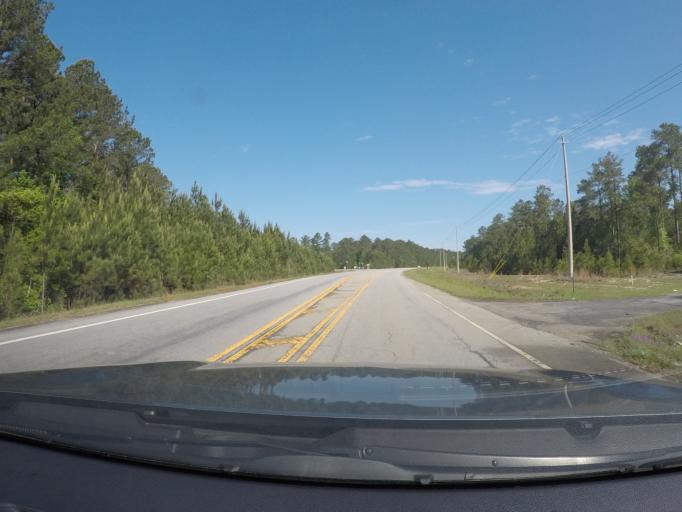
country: US
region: Georgia
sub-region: Chatham County
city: Bloomingdale
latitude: 32.0631
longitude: -81.3156
